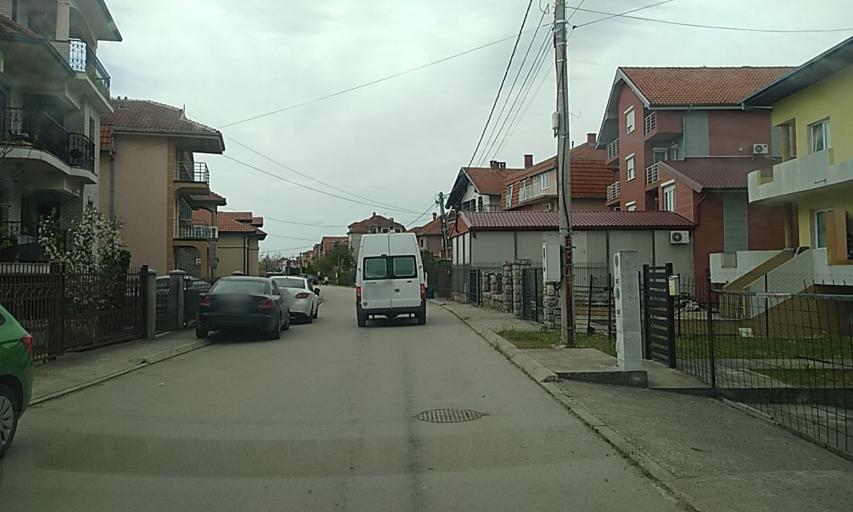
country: RS
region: Central Serbia
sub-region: Nisavski Okrug
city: Nis
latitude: 43.3349
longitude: 21.9350
